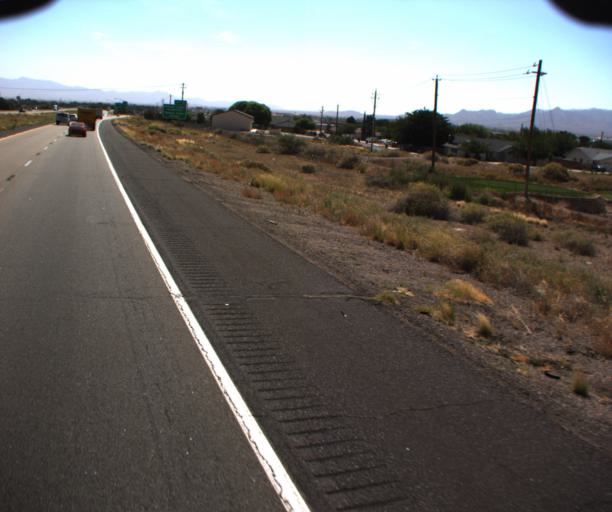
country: US
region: Arizona
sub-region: Mohave County
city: Kingman
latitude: 35.2152
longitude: -114.0448
